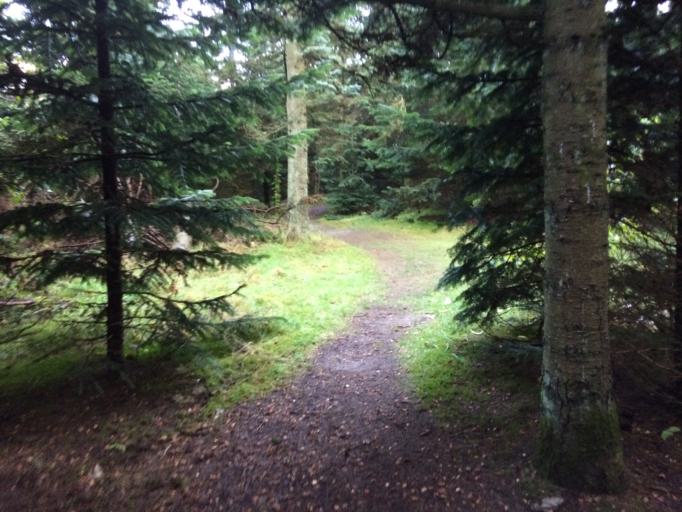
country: DK
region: Central Jutland
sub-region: Herning Kommune
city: Kibaek
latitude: 55.9248
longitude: 8.9108
